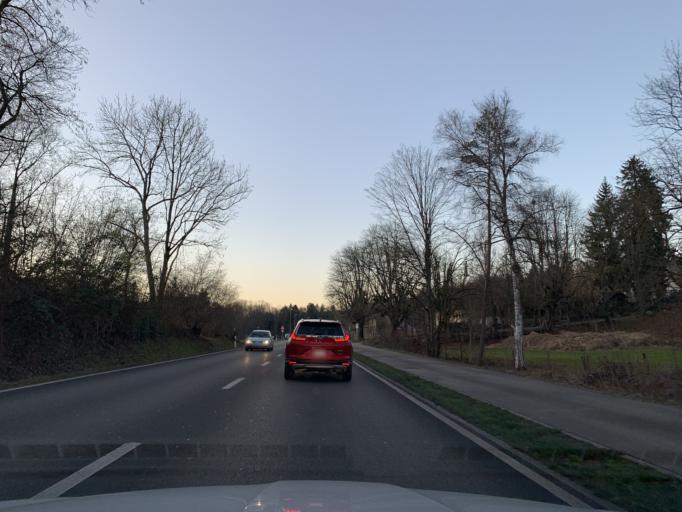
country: CH
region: Zurich
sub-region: Bezirk Dielsdorf
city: Regensdorf
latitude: 47.4311
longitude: 8.4850
